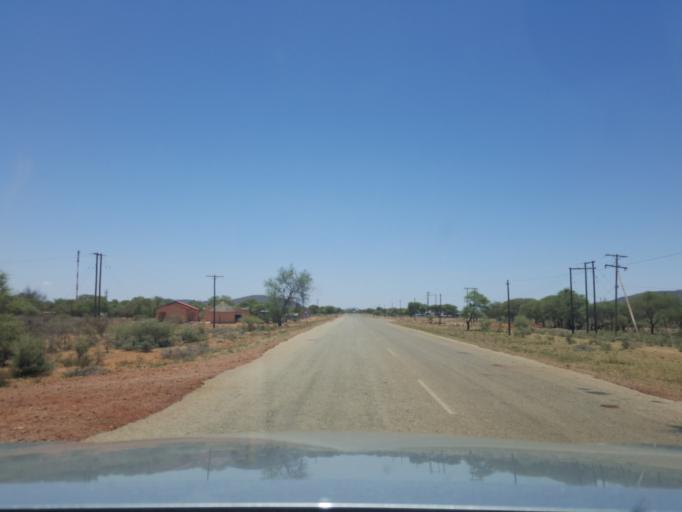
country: BW
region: South East
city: Ramotswa
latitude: -24.9889
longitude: 25.8975
